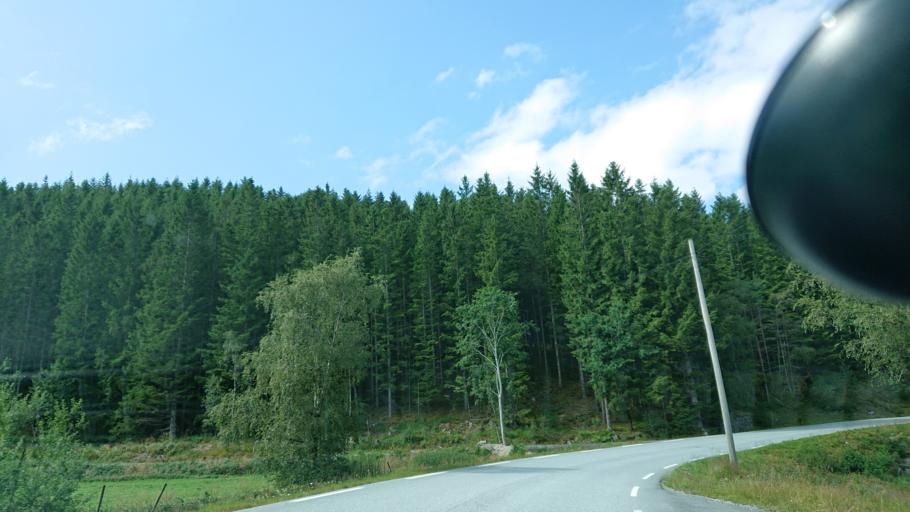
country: NO
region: Rogaland
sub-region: Hjelmeland
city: Hjelmelandsvagen
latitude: 59.2412
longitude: 6.2913
